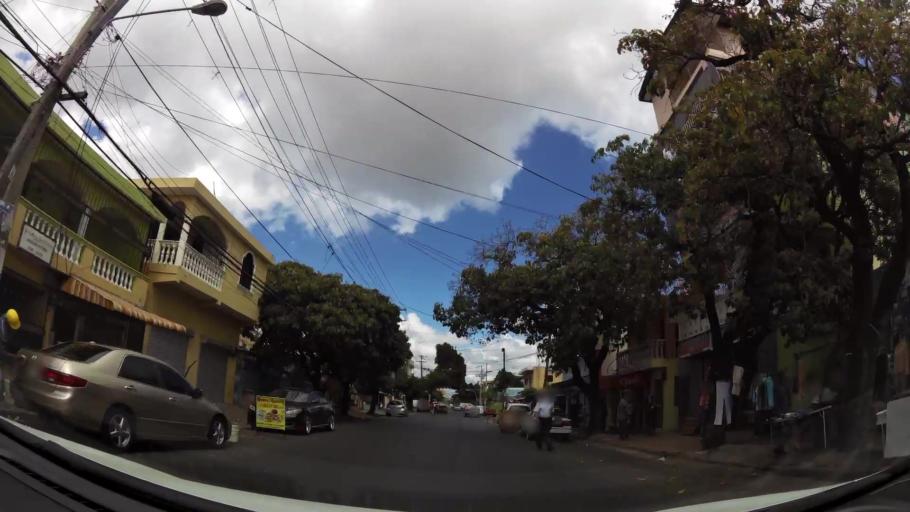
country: DO
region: Nacional
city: Ensanche Luperon
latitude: 18.5012
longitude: -69.8941
